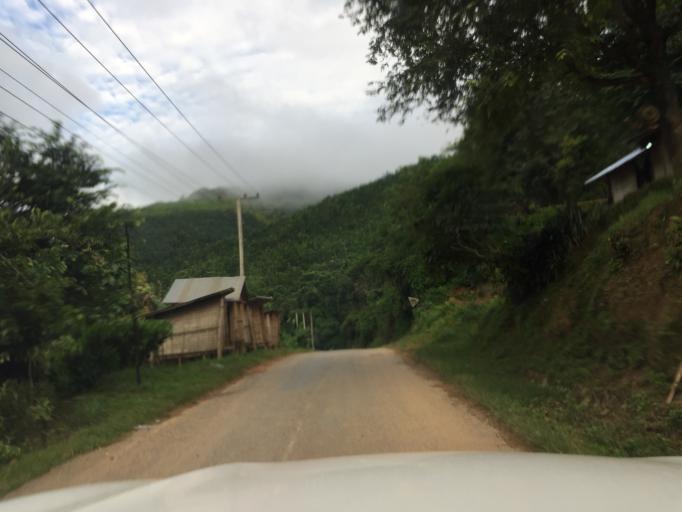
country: LA
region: Phongsali
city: Khoa
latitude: 21.1035
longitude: 102.2875
